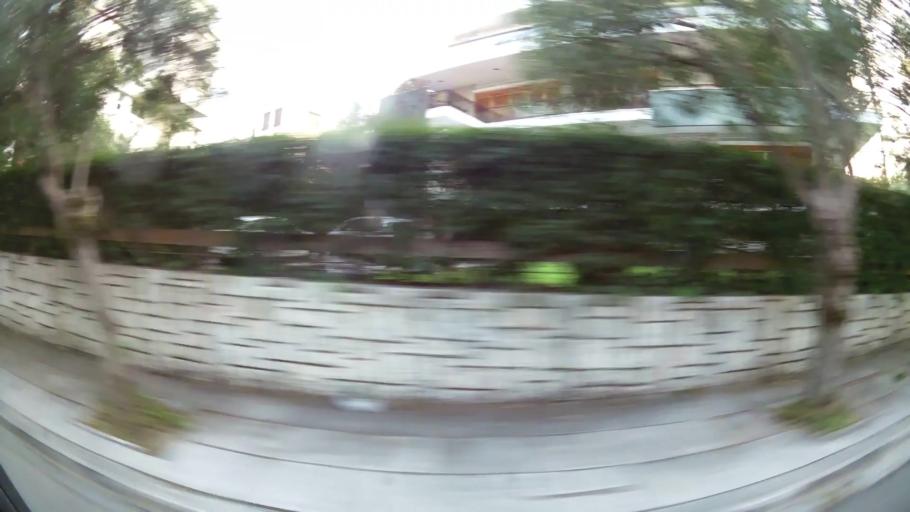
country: GR
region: Attica
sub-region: Nomarchia Athinas
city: Filothei
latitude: 38.0205
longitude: 23.7792
